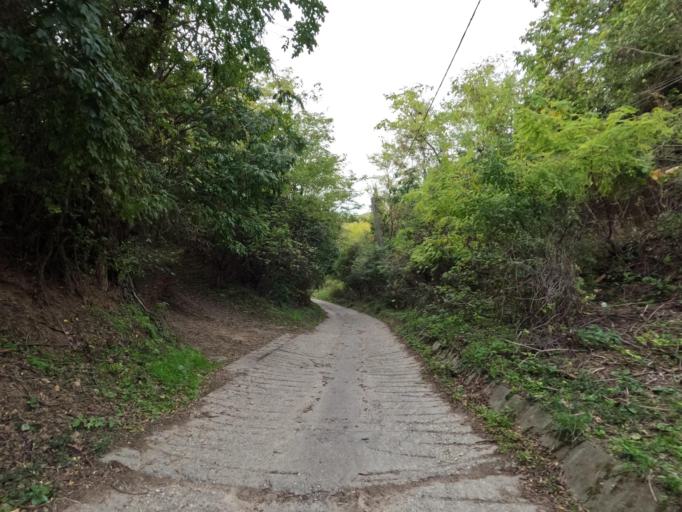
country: HU
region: Tolna
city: Szekszard
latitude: 46.3483
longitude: 18.6754
